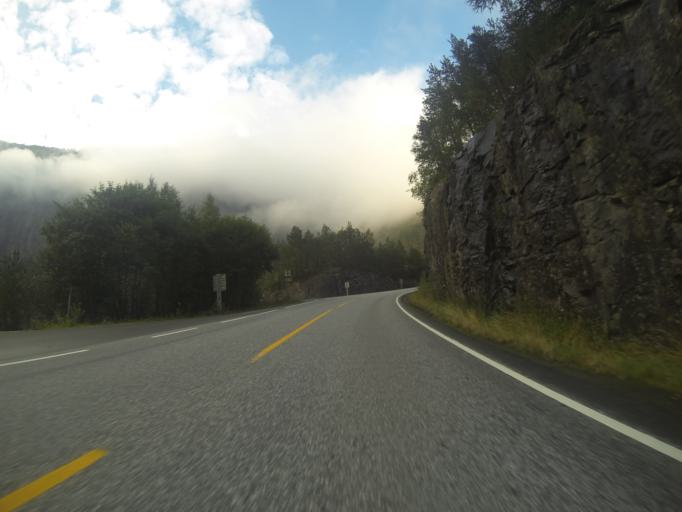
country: NO
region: Rogaland
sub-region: Sauda
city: Sauda
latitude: 59.8746
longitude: 6.4039
